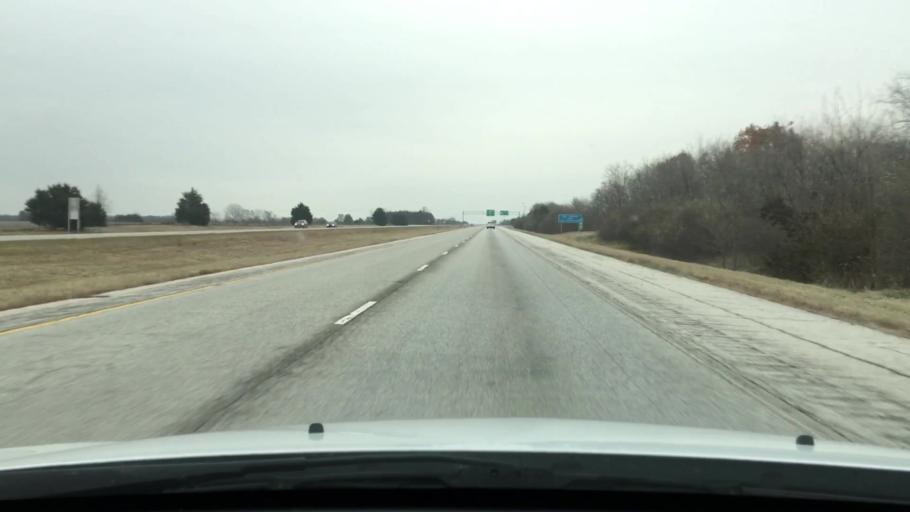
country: US
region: Illinois
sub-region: Morgan County
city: South Jacksonville
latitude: 39.6802
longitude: -90.3071
